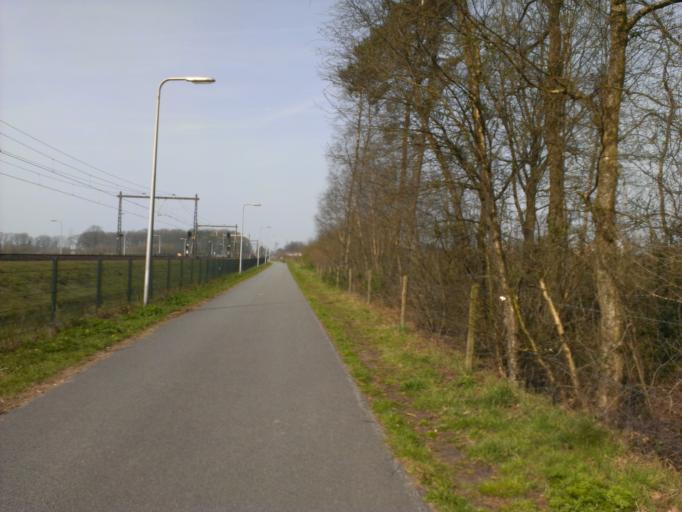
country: NL
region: Overijssel
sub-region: Gemeente Almelo
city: Almelo
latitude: 52.3368
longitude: 6.6767
